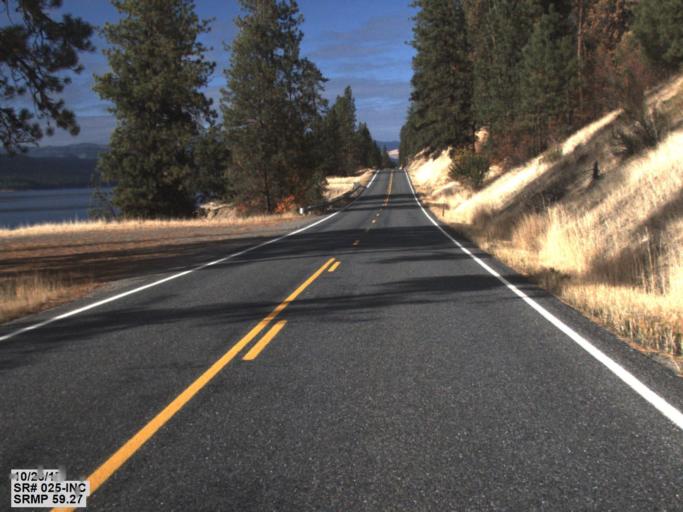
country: US
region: Washington
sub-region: Stevens County
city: Kettle Falls
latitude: 48.3282
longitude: -118.1535
